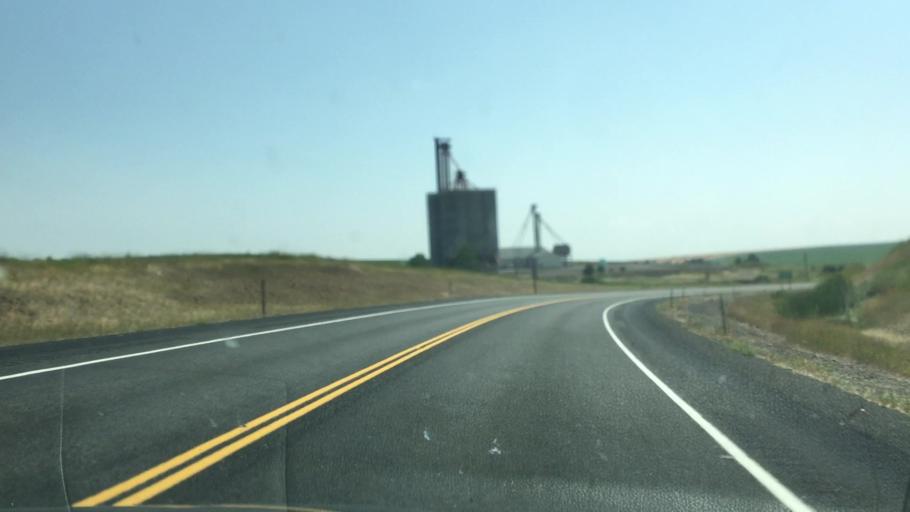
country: US
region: Idaho
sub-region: Lewis County
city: Nezperce
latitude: 46.2371
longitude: -116.4682
